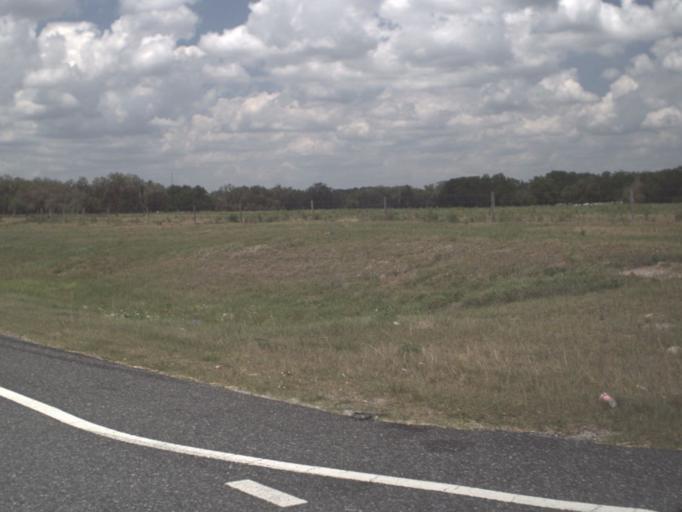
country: US
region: Florida
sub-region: Sumter County
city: Wildwood
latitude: 28.8439
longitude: -82.0296
